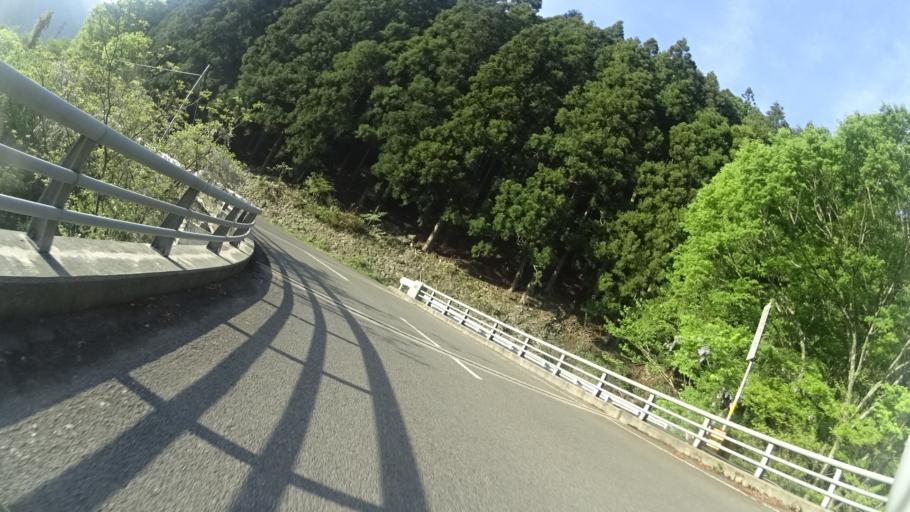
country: JP
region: Tokushima
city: Ikedacho
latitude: 33.9154
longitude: 133.8243
